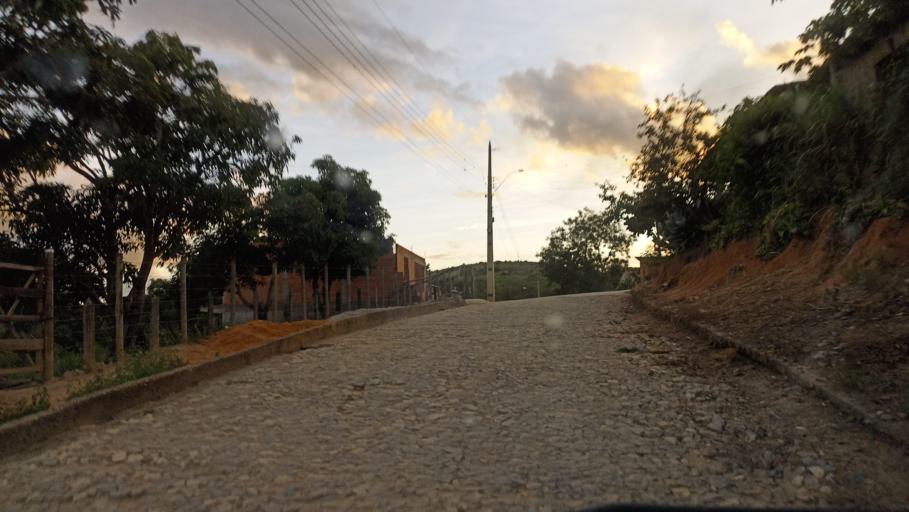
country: BR
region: Minas Gerais
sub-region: Almenara
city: Almenara
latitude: -16.5223
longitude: -40.4416
